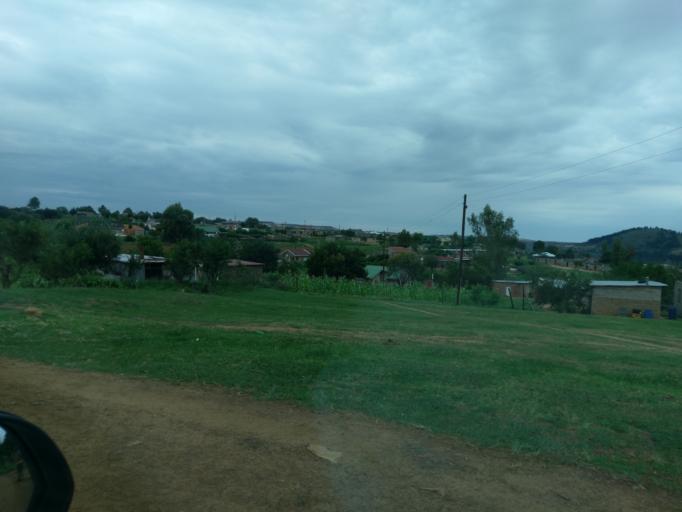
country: LS
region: Berea
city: Teyateyaneng
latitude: -29.1151
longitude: 27.9666
